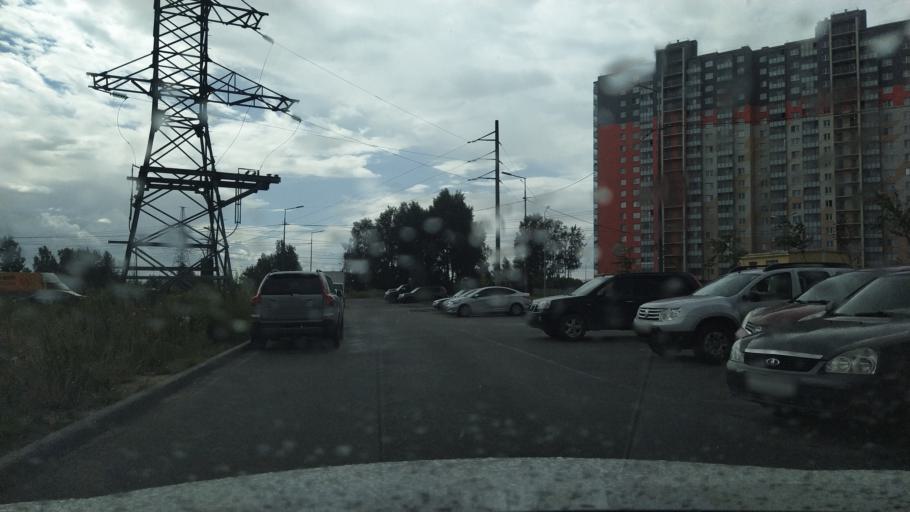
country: RU
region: Leningrad
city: Murino
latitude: 60.0270
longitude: 30.4567
